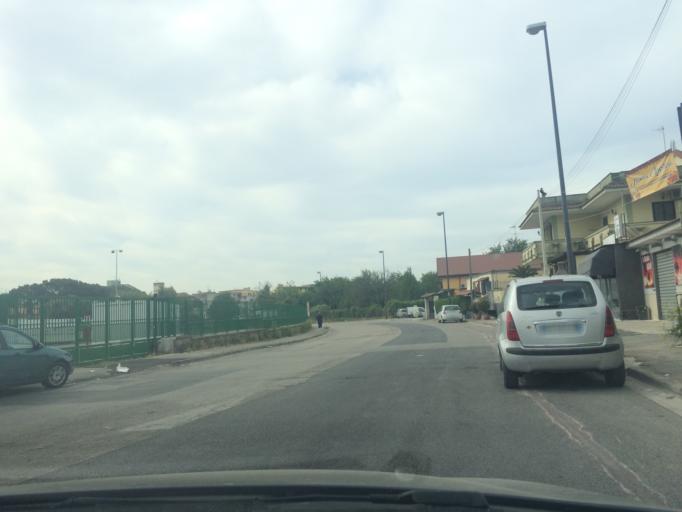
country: IT
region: Campania
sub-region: Provincia di Napoli
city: Mugnano di Napoli
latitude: 40.8939
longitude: 14.2267
